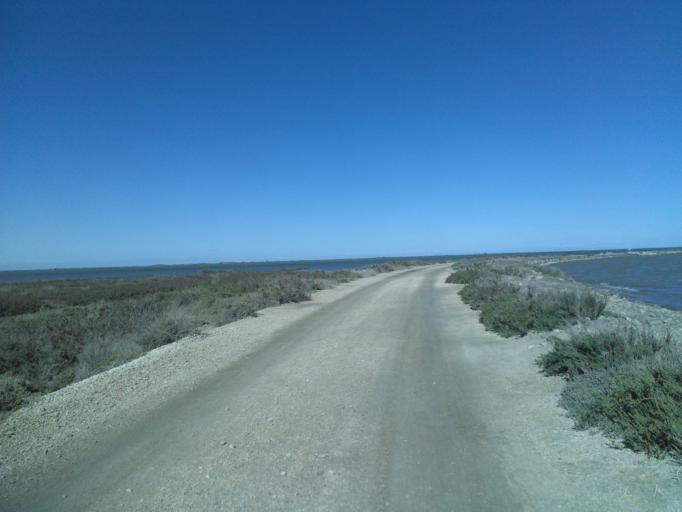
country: FR
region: Provence-Alpes-Cote d'Azur
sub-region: Departement des Bouches-du-Rhone
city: Saintes-Maries-de-la-Mer
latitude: 43.4186
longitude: 4.6206
